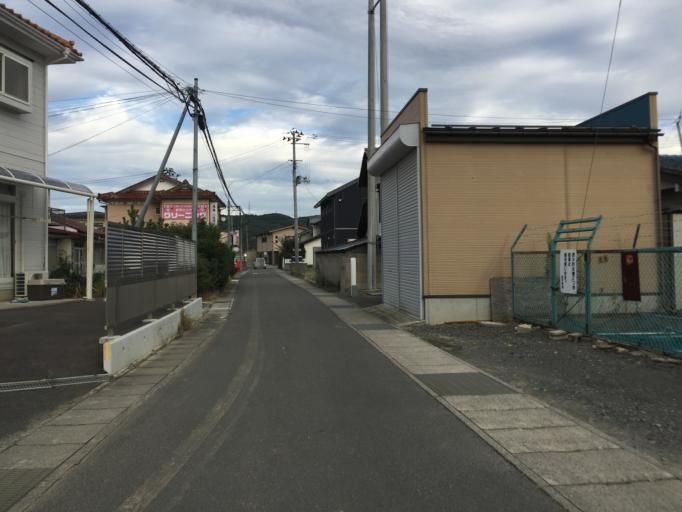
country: JP
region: Fukushima
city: Fukushima-shi
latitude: 37.7780
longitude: 140.4991
